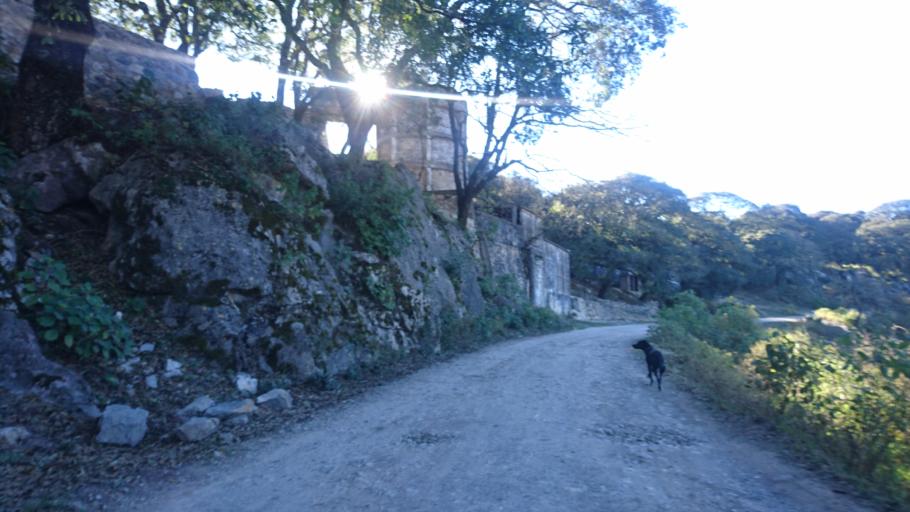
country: MX
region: San Luis Potosi
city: Zaragoza
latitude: 22.0305
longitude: -100.6081
